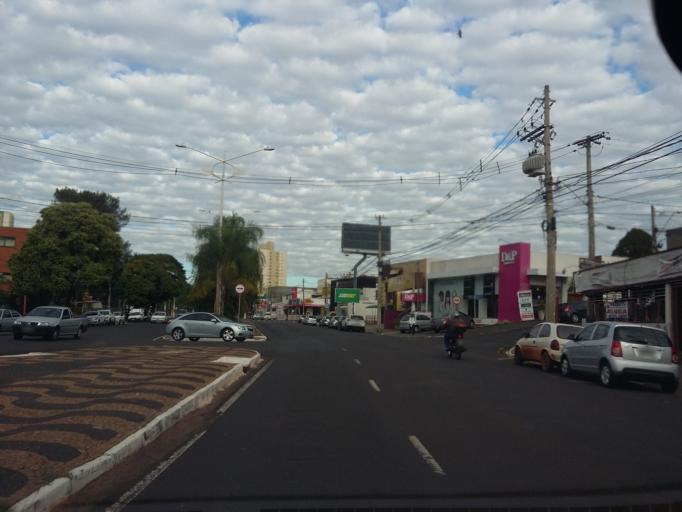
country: BR
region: Sao Paulo
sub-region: Sao Jose Do Rio Preto
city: Sao Jose do Rio Preto
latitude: -20.8126
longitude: -49.3886
